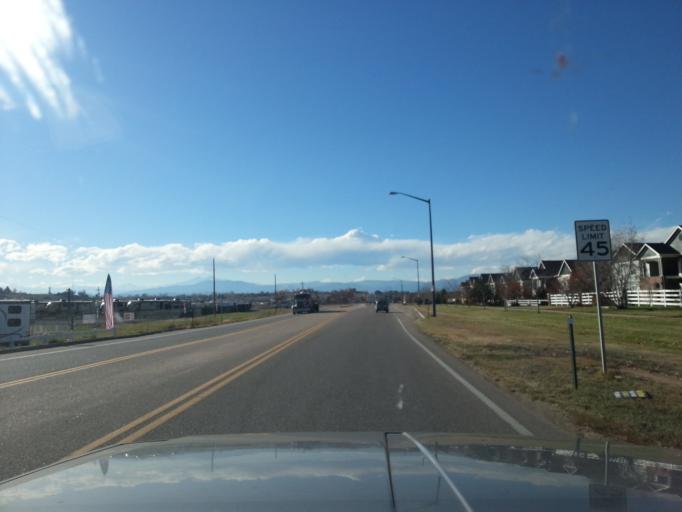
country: US
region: Colorado
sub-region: Larimer County
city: Loveland
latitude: 40.3784
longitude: -105.0658
